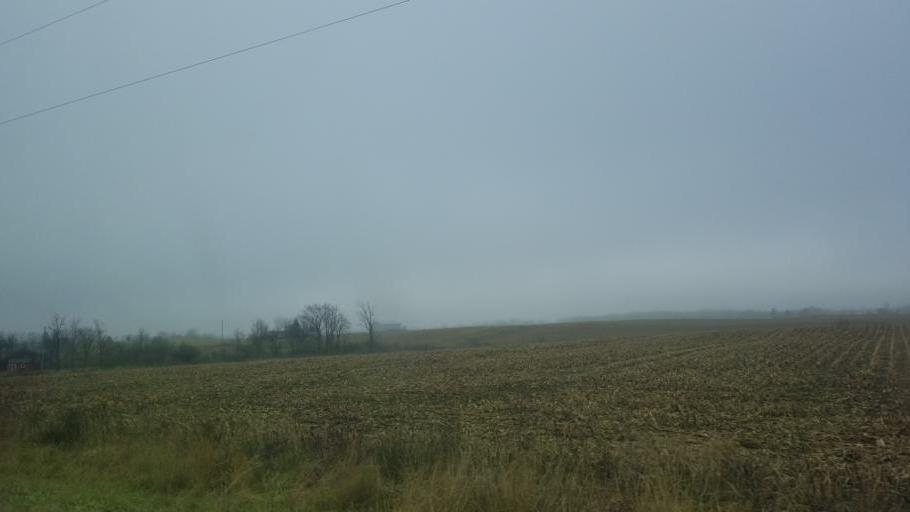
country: US
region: Ohio
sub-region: Champaign County
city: North Lewisburg
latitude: 40.2680
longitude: -83.5923
